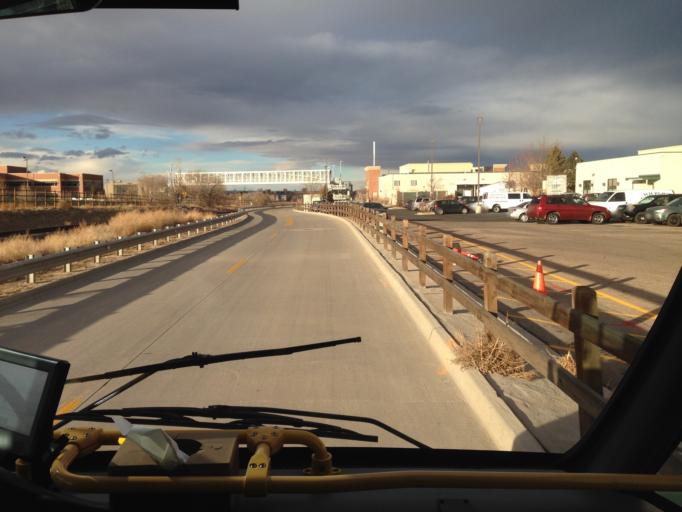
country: US
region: Colorado
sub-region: Larimer County
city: Fort Collins
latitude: 40.5579
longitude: -105.0796
